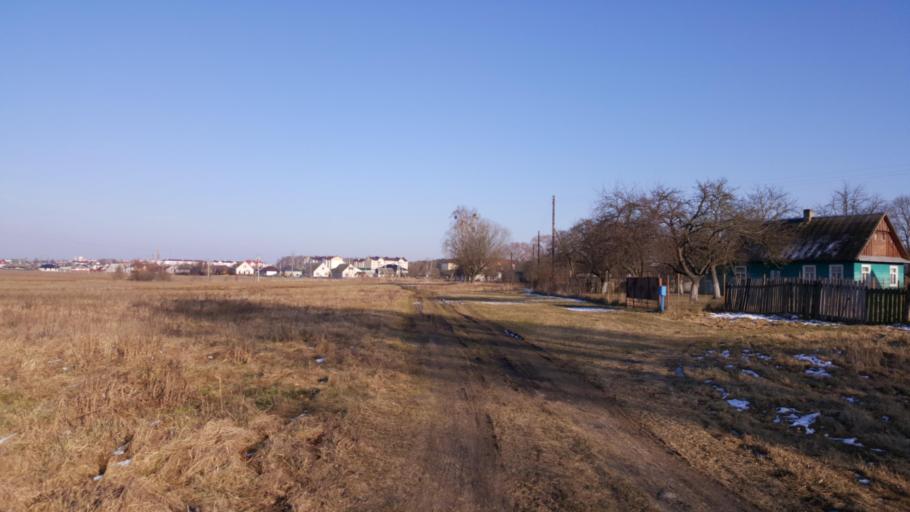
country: BY
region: Brest
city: Kamyanyets
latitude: 52.3867
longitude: 23.8058
